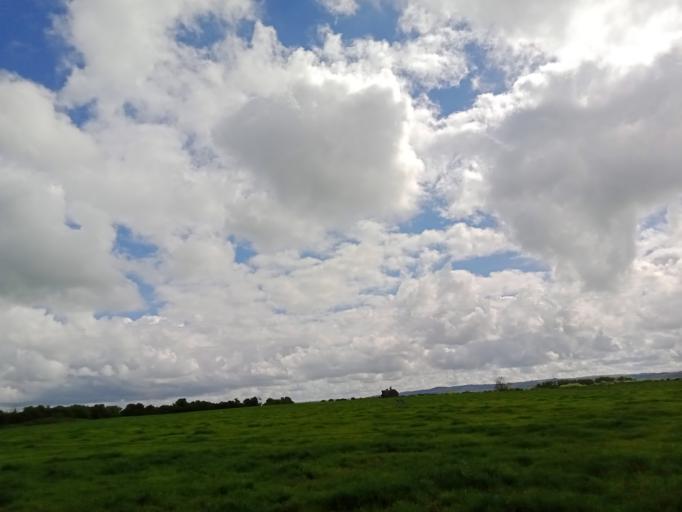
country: IE
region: Munster
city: Thurles
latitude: 52.6695
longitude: -7.6742
